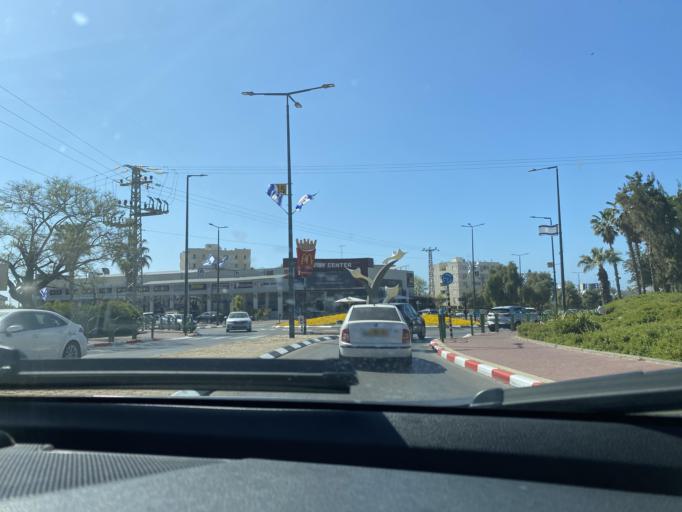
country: IL
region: Southern District
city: Ashqelon
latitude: 31.6808
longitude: 34.5712
